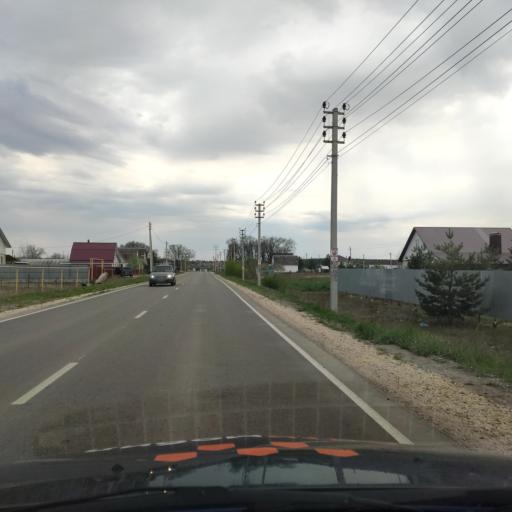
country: RU
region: Voronezj
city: Podgornoye
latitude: 51.8757
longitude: 39.1734
